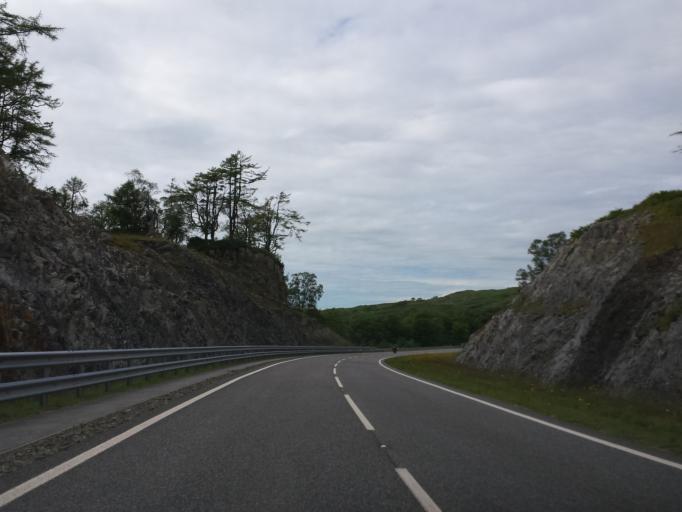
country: GB
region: Scotland
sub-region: Argyll and Bute
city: Isle Of Mull
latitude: 56.9067
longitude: -5.8207
